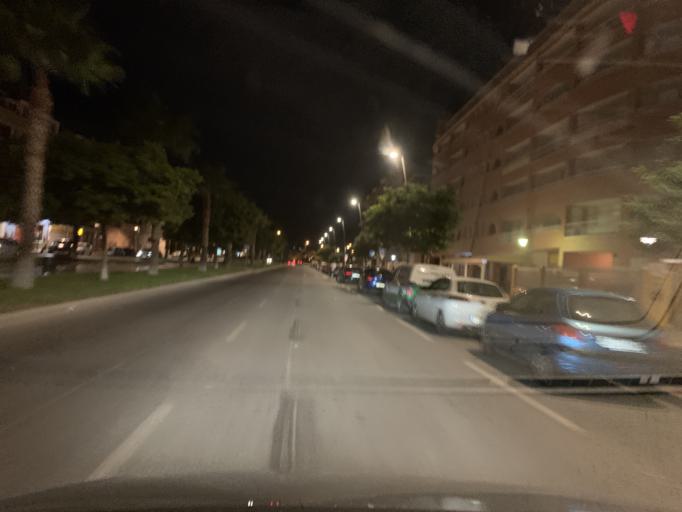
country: ES
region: Andalusia
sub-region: Provincia de Almeria
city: Roquetas de Mar
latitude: 36.7766
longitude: -2.6081
